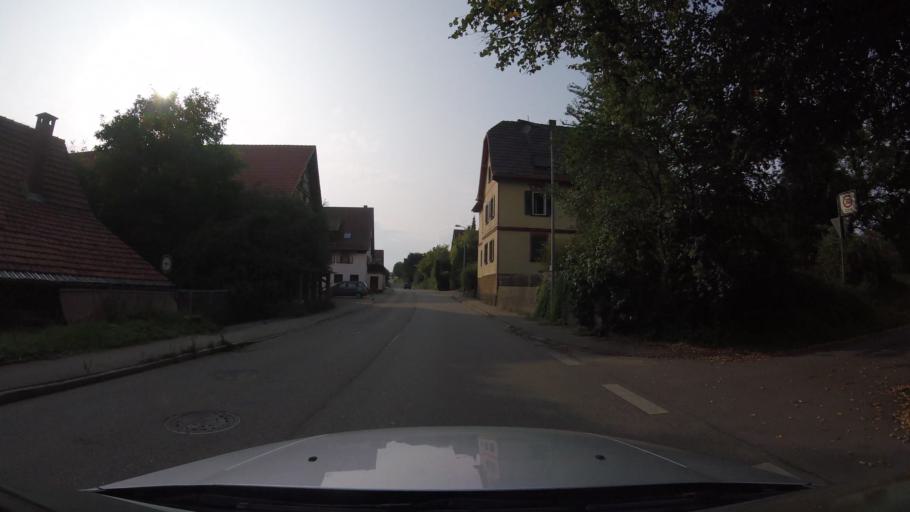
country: DE
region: Baden-Wuerttemberg
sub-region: Regierungsbezirk Stuttgart
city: Alfdorf
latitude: 48.8414
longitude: 9.6806
